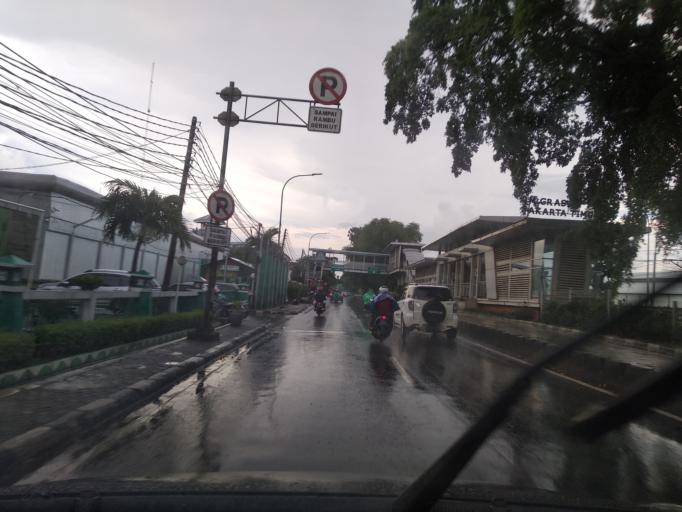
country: ID
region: Jakarta Raya
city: Jakarta
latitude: -6.2147
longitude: 106.8828
